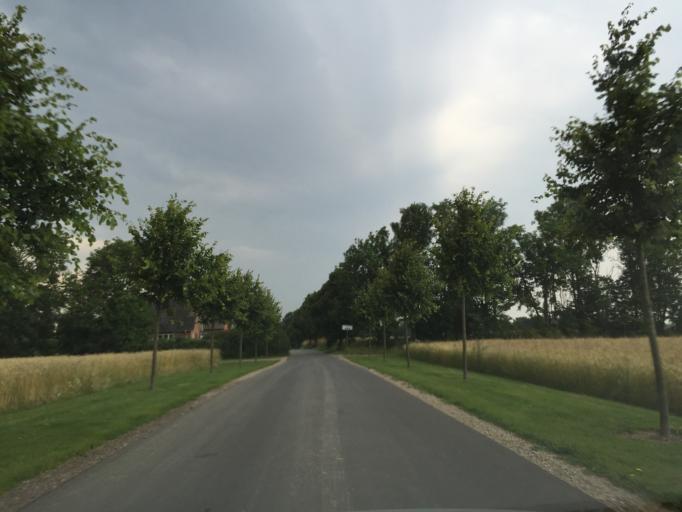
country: DK
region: Central Jutland
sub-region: Viborg Kommune
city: Bjerringbro
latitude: 56.3347
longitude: 9.6418
